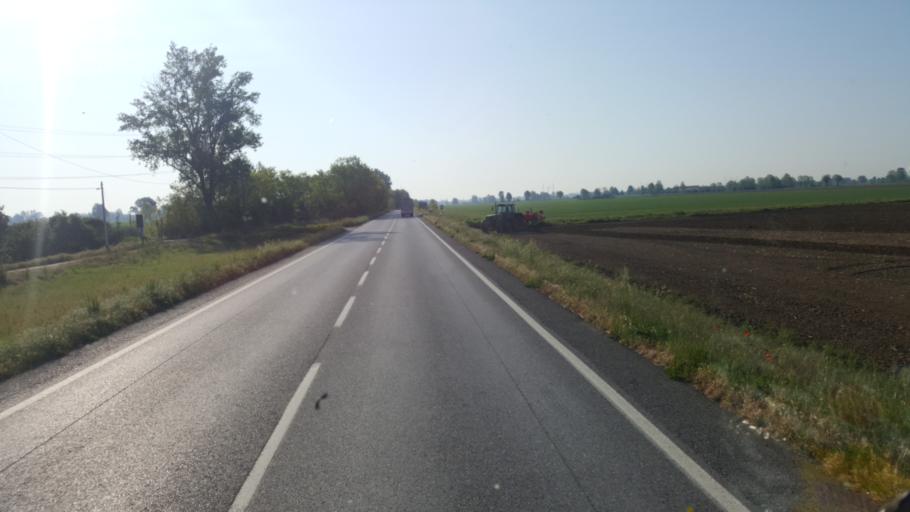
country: IT
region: Lombardy
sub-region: Provincia di Cremona
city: Sesto ed Uniti
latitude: 45.1922
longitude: 9.9254
